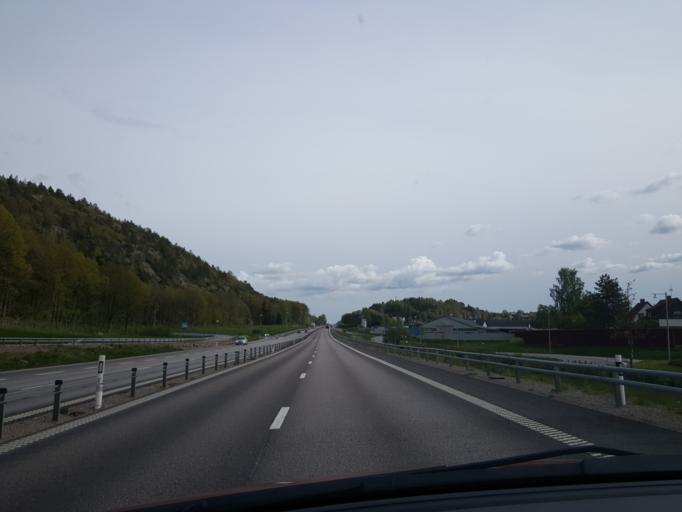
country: SE
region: Vaestra Goetaland
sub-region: Lilla Edets Kommun
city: Lilla Edet
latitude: 58.1475
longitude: 12.1349
